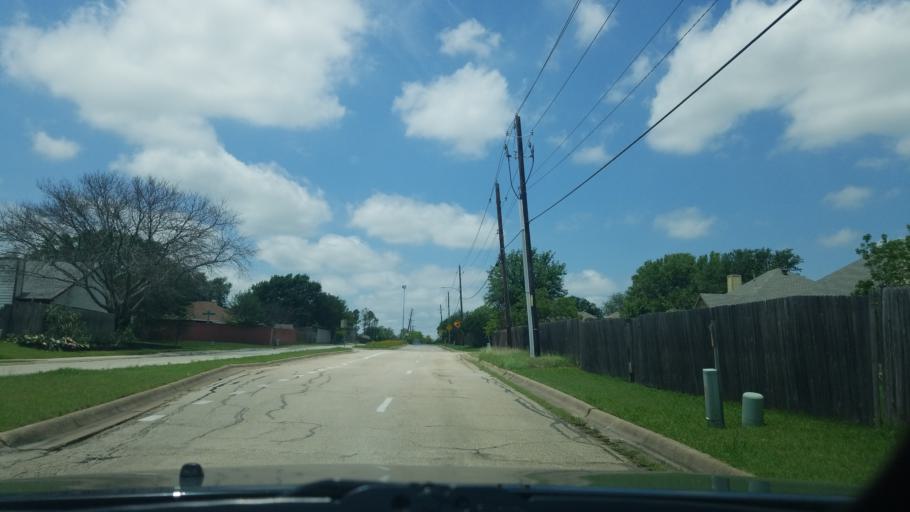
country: US
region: Texas
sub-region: Denton County
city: Denton
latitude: 33.2398
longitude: -97.1673
